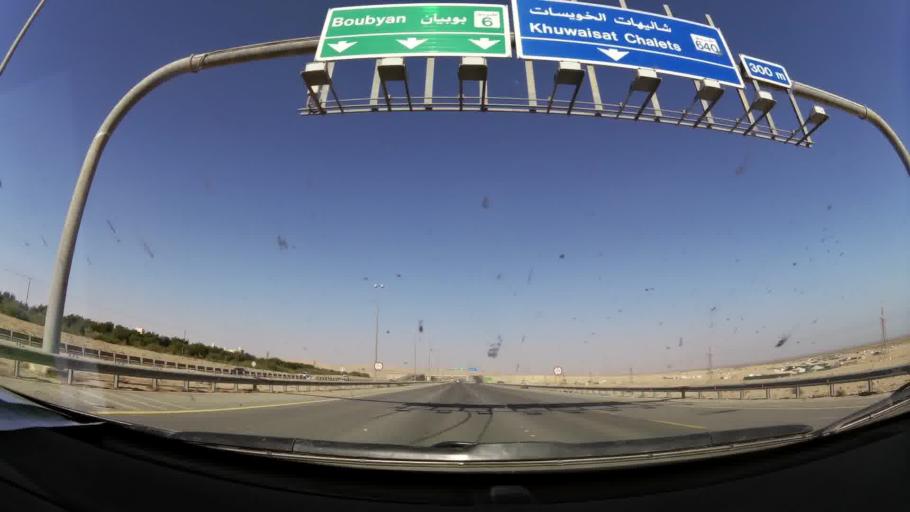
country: KW
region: Muhafazat al Jahra'
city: Al Jahra'
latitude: 29.4682
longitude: 47.7654
